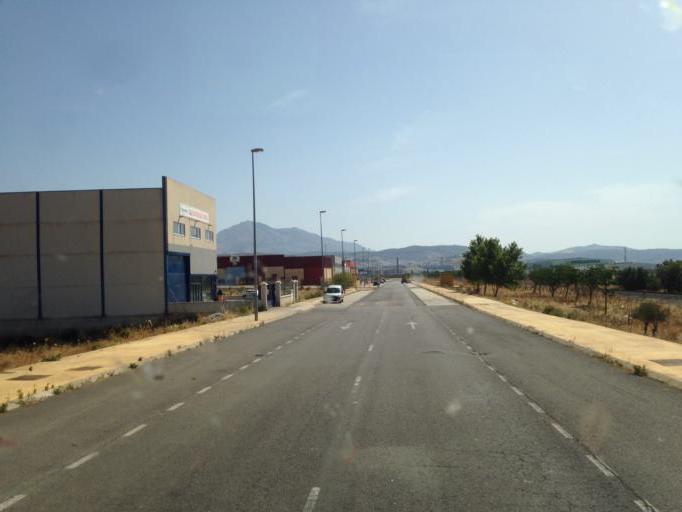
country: ES
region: Andalusia
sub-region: Provincia de Malaga
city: Antequera
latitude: 37.0415
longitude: -4.5201
